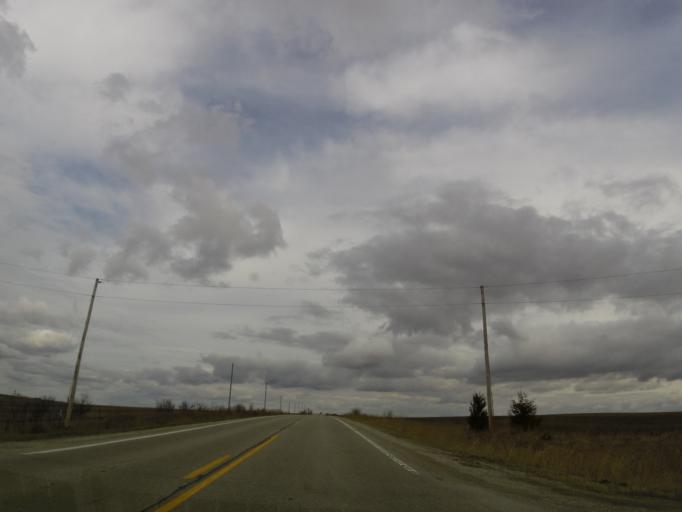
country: US
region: Iowa
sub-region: Black Hawk County
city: Waterloo
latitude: 42.5704
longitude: -92.2979
